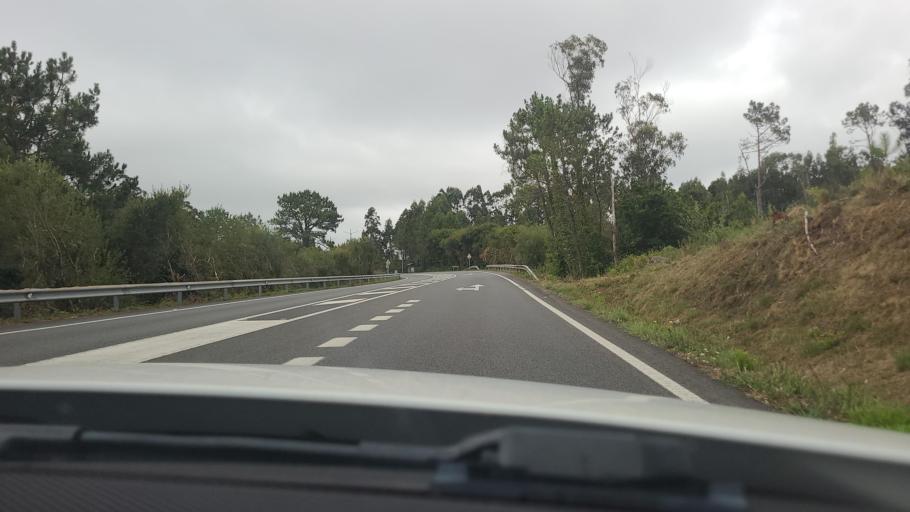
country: ES
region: Galicia
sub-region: Provincia da Coruna
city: Cee
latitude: 43.0079
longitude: -9.1701
